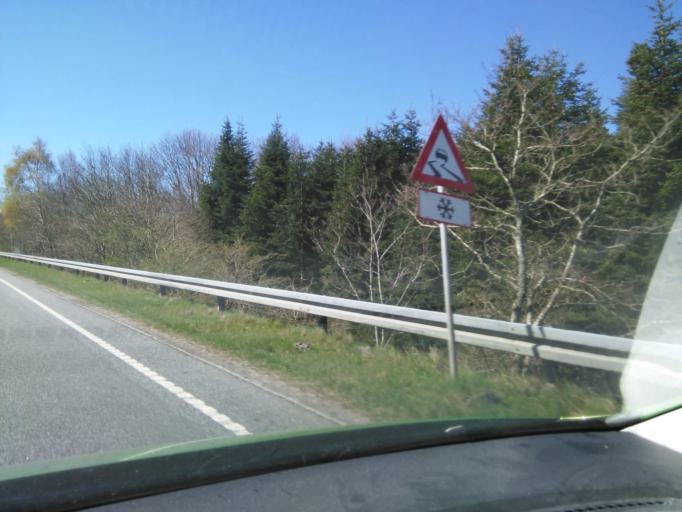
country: DK
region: South Denmark
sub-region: Varde Kommune
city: Varde
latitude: 55.6814
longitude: 8.5856
